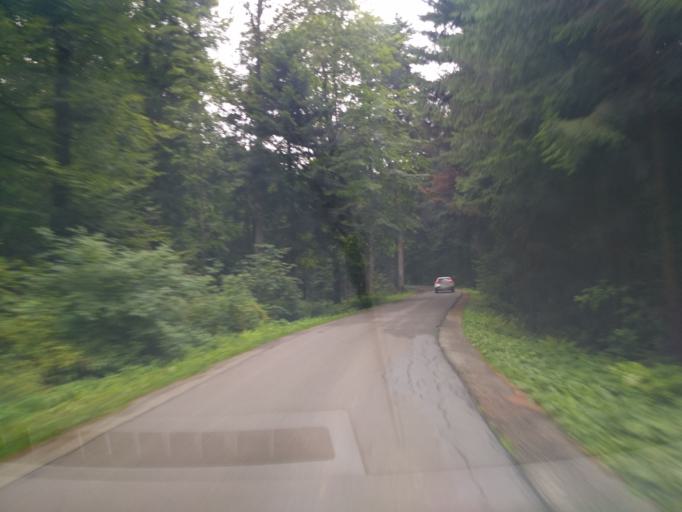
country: PL
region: Subcarpathian Voivodeship
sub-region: Powiat strzyzowski
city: Strzyzow
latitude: 49.8997
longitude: 21.7854
